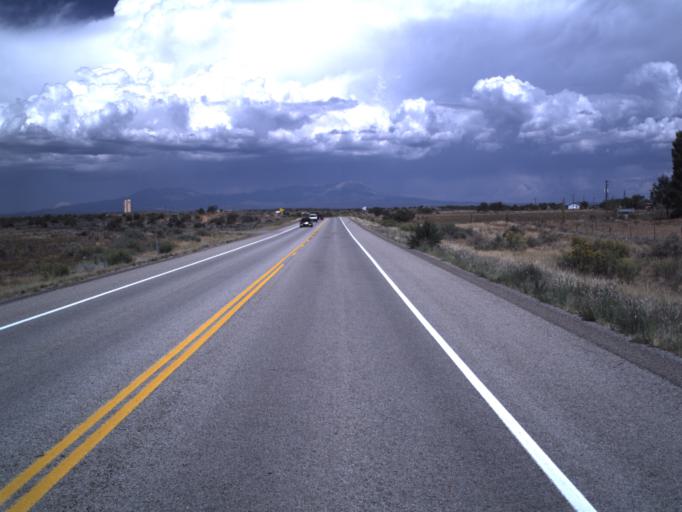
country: US
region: Utah
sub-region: San Juan County
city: Blanding
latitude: 37.4699
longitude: -109.4669
